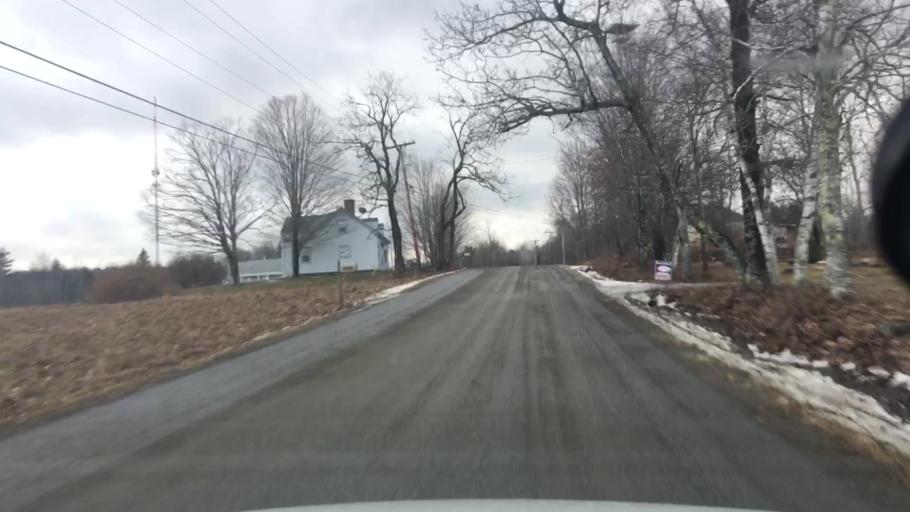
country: US
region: Maine
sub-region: Penobscot County
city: Orrington
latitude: 44.6831
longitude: -68.7543
